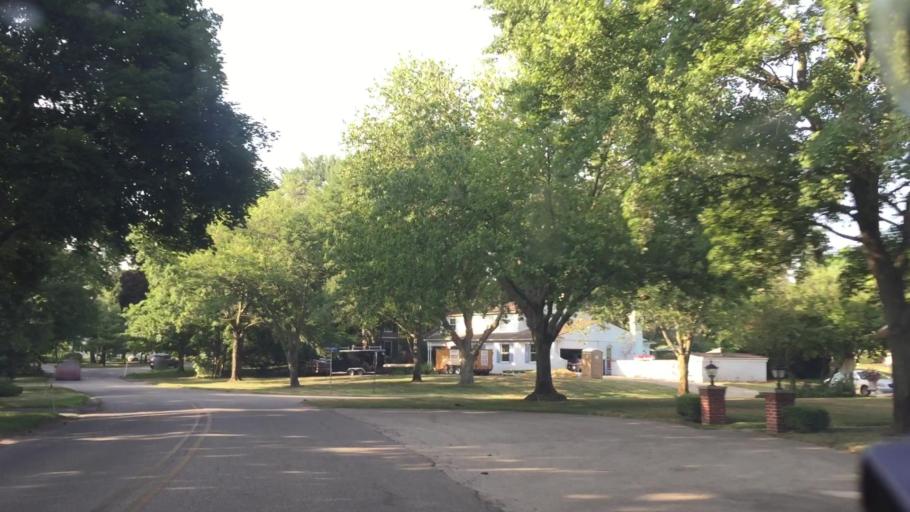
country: US
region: Michigan
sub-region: Oakland County
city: Beverly Hills
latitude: 42.5288
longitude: -83.2361
